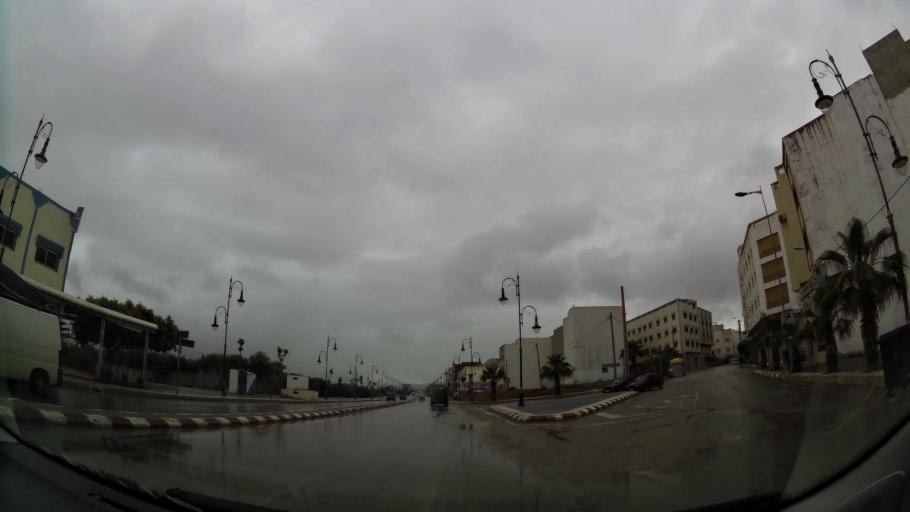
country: MA
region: Taza-Al Hoceima-Taounate
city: Imzourene
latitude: 35.1421
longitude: -3.8482
